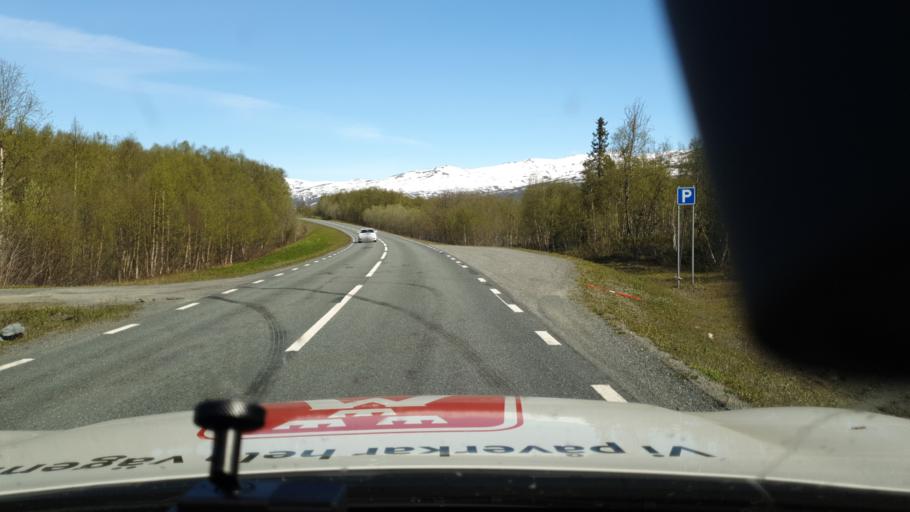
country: NO
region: Nordland
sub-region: Rana
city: Mo i Rana
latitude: 65.7603
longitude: 15.1162
